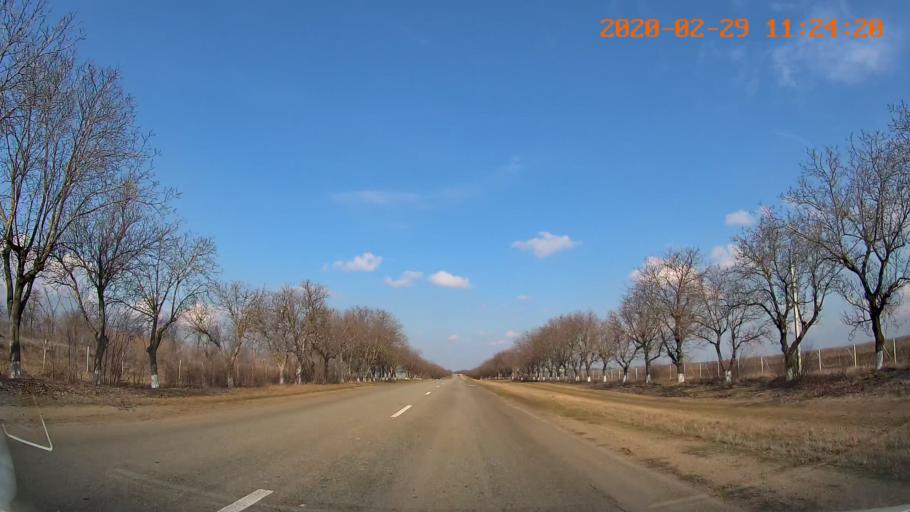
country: MD
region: Telenesti
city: Cocieri
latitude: 47.4220
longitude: 29.1551
